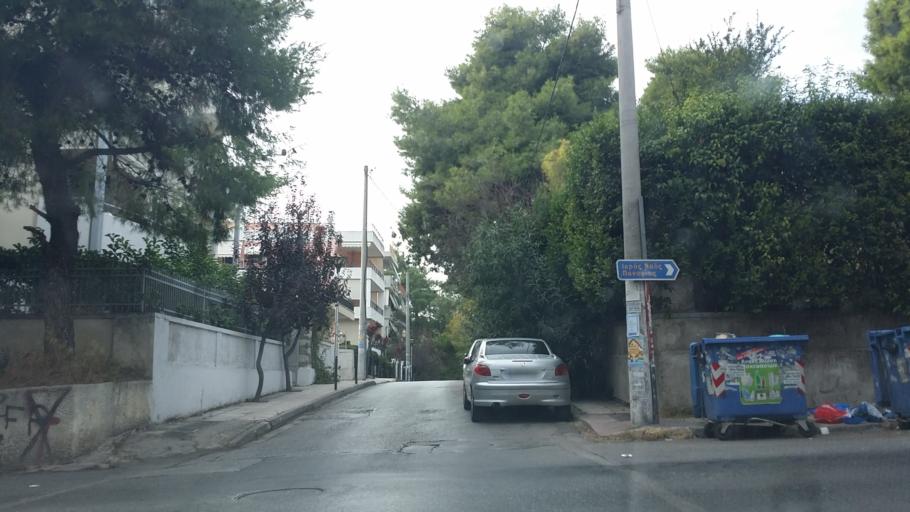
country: GR
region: Attica
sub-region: Nomarchia Athinas
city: Irakleio
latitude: 38.0464
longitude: 23.7721
